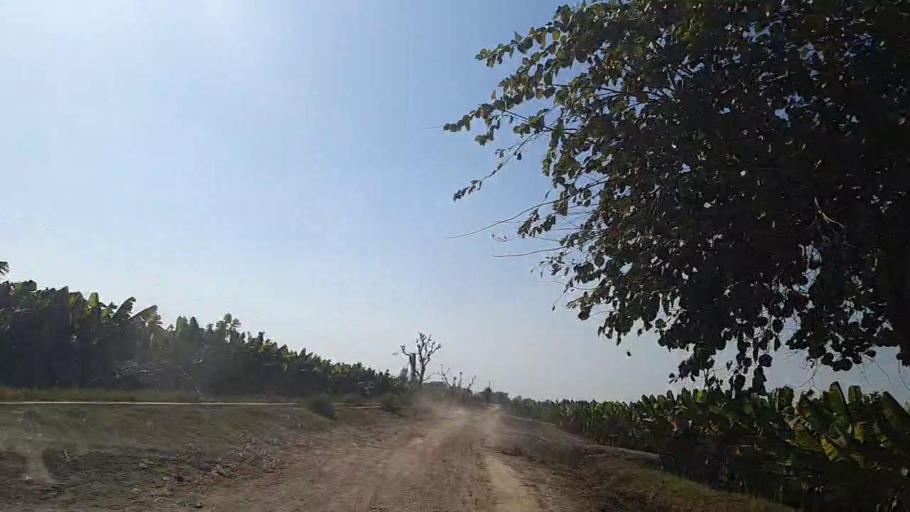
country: PK
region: Sindh
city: Sakrand
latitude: 26.2333
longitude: 68.1756
